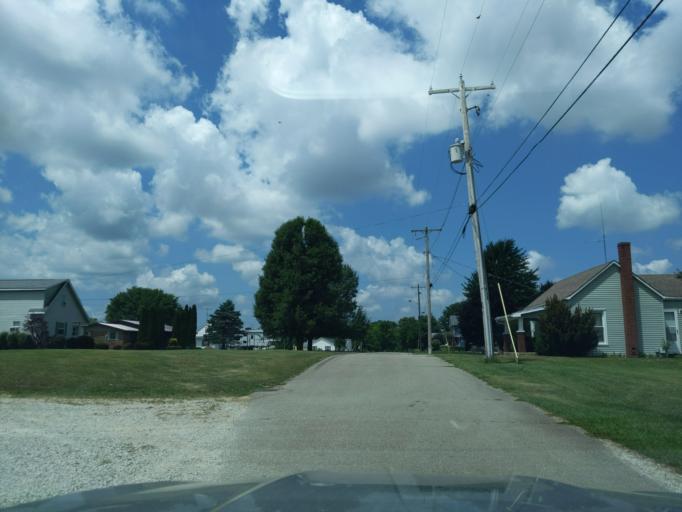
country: US
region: Indiana
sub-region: Ripley County
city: Osgood
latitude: 39.2027
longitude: -85.3280
